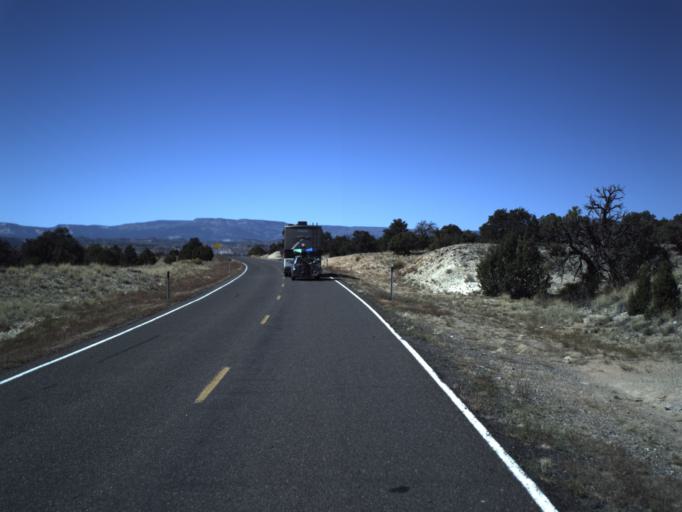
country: US
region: Utah
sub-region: Wayne County
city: Loa
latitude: 37.7372
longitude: -111.5461
